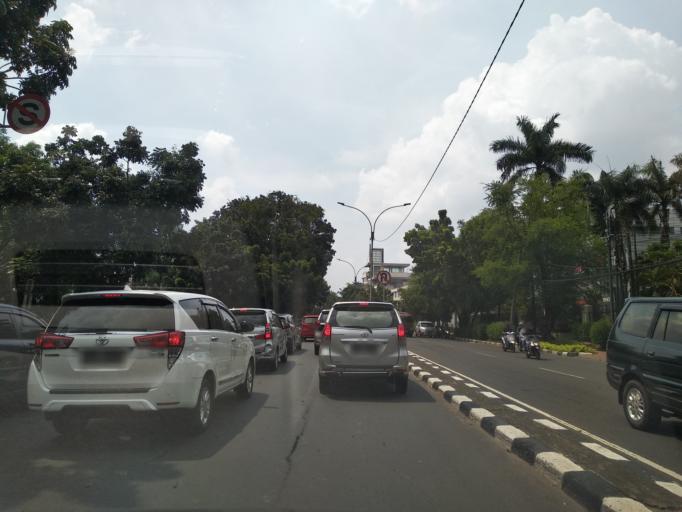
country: ID
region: Jakarta Raya
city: Jakarta
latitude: -6.2281
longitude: 106.8474
